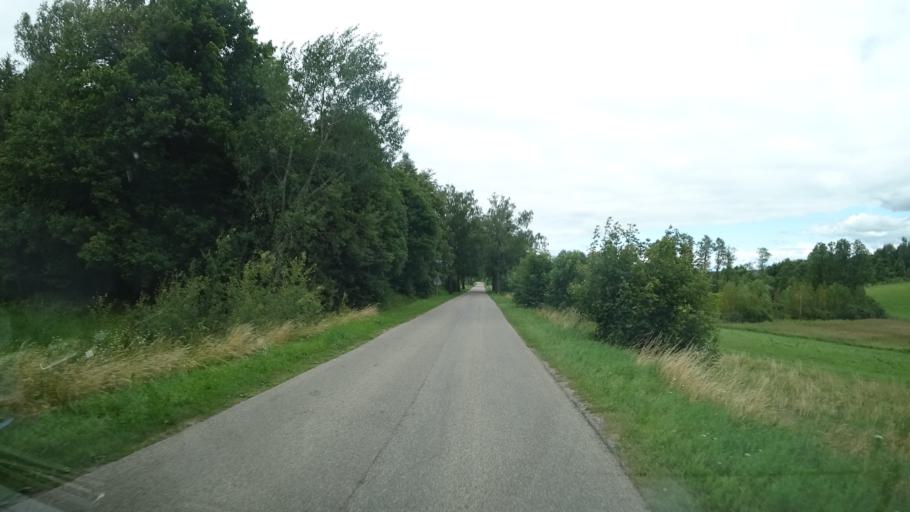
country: PL
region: Podlasie
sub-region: Powiat suwalski
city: Filipow
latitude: 54.2877
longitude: 22.5705
